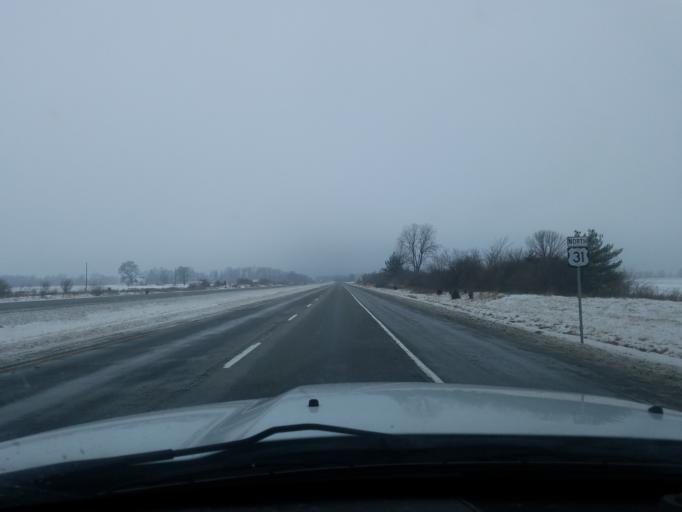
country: US
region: Indiana
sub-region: Fulton County
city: Rochester
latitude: 40.9965
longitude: -86.1677
